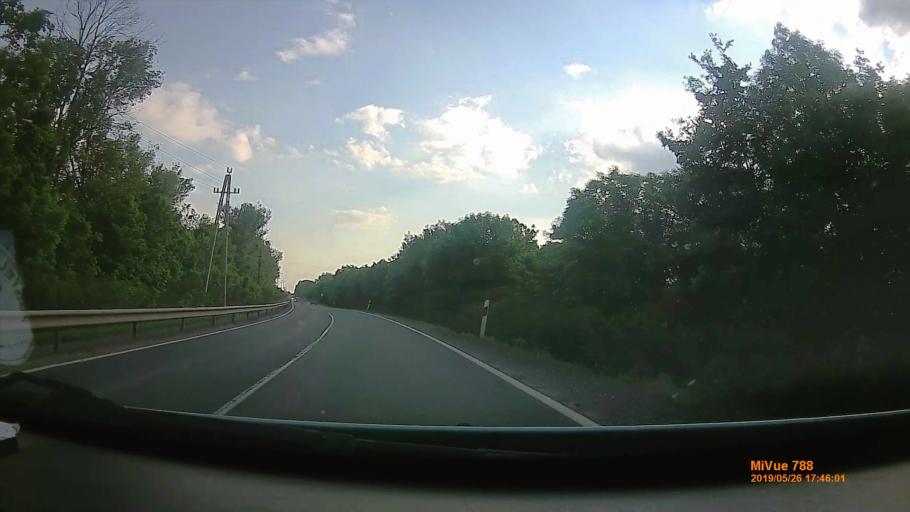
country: HU
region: Borsod-Abauj-Zemplen
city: Szikszo
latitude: 48.2121
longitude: 20.9420
